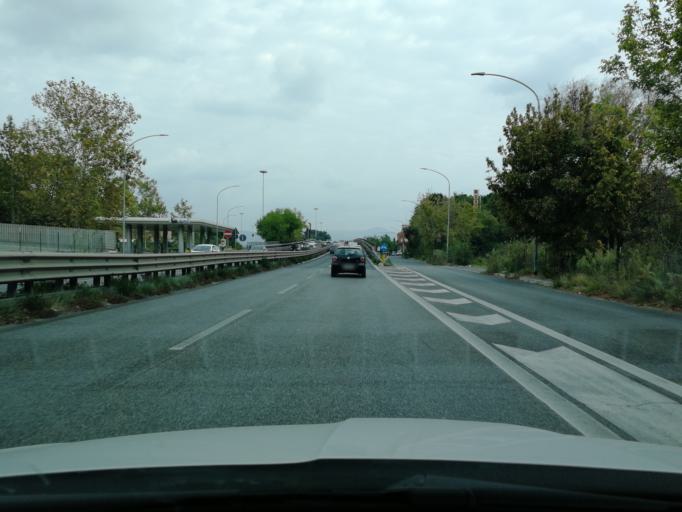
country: IT
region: Latium
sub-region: Citta metropolitana di Roma Capitale
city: Ciampino
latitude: 41.8447
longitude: 12.5811
